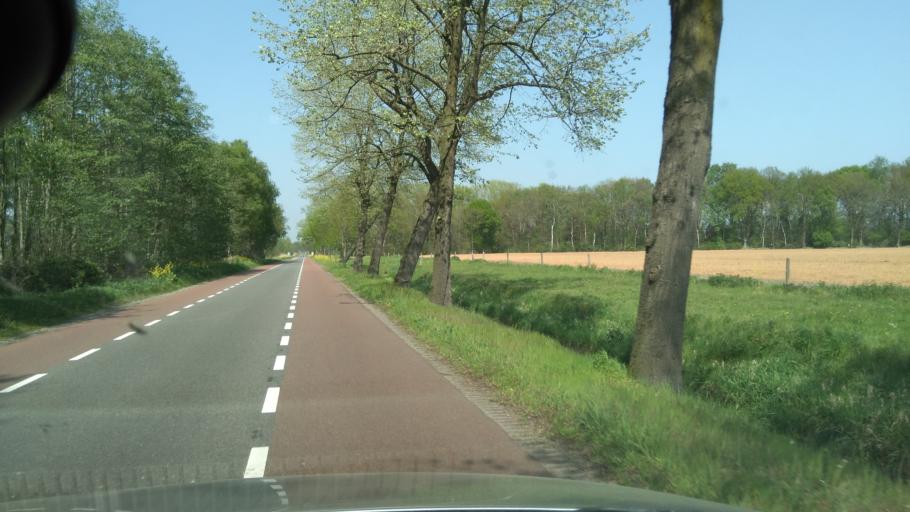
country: NL
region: North Brabant
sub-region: Gemeente Baarle-Nassau
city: Baarle-Nassau
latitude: 51.4755
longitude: 4.8602
